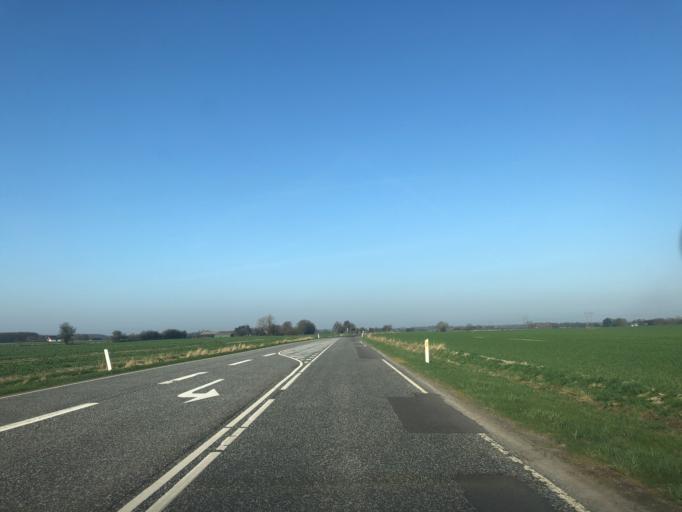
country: DK
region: Zealand
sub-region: Stevns Kommune
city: Harlev
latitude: 55.2782
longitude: 12.2544
